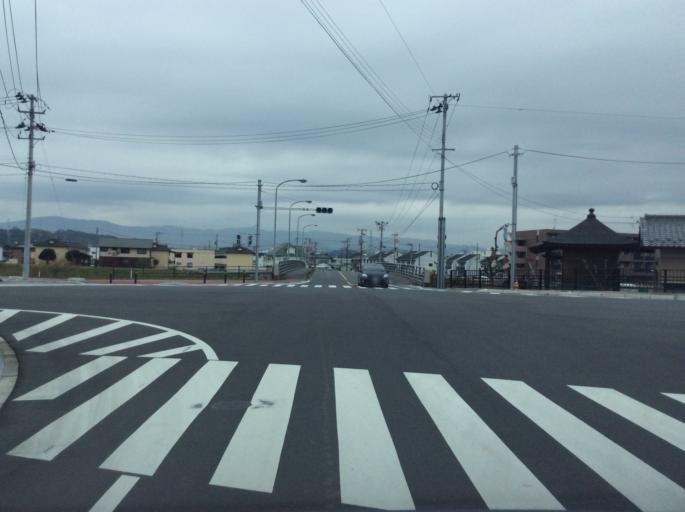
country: JP
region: Fukushima
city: Iwaki
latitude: 37.0495
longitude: 140.9137
